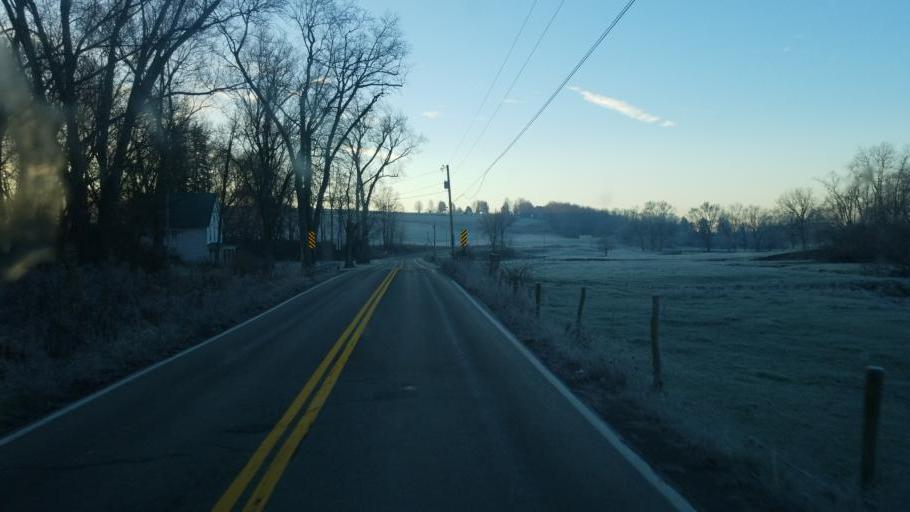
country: US
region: Ohio
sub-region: Wayne County
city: Apple Creek
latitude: 40.6870
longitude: -81.8653
